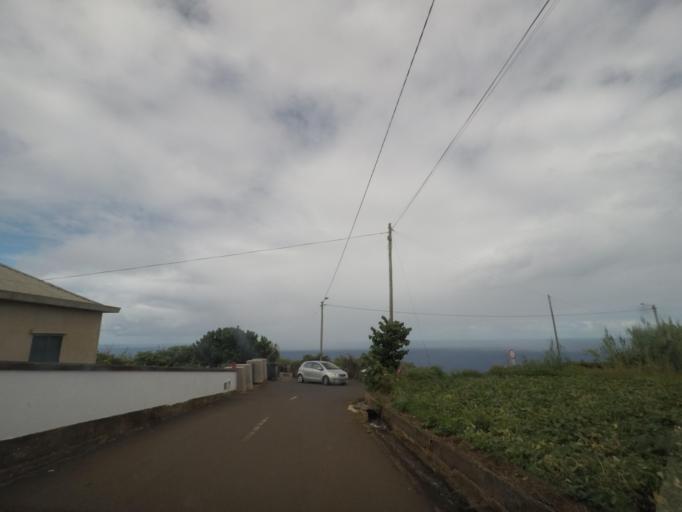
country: PT
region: Madeira
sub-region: Santana
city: Santana
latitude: 32.8342
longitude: -16.9061
